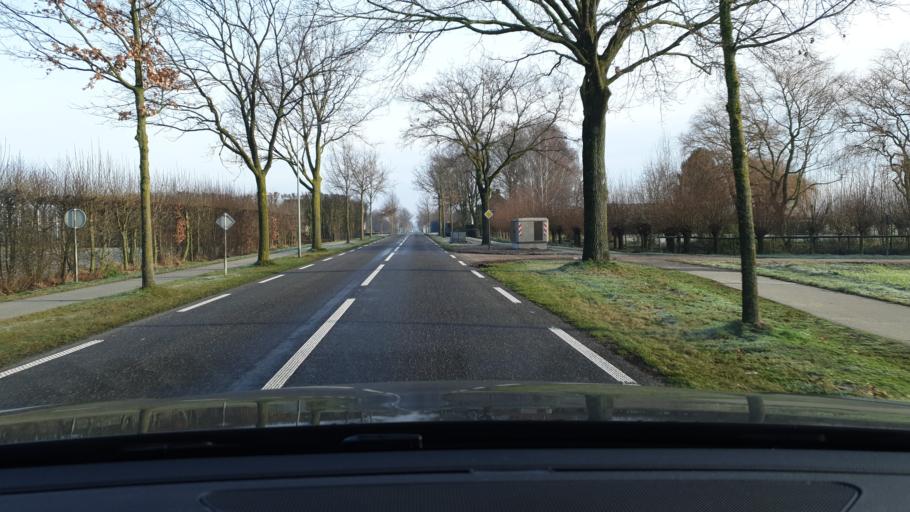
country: NL
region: Limburg
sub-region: Gemeente Peel en Maas
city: Maasbree
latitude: 51.3859
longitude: 5.9984
